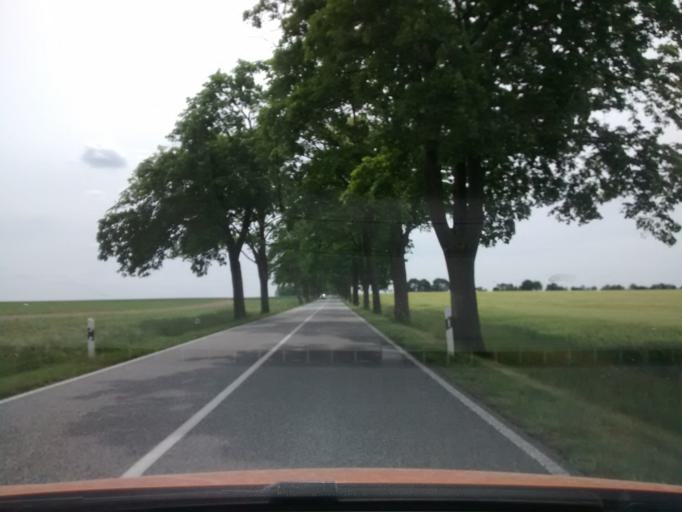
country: DE
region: Brandenburg
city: Juterbog
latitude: 51.9497
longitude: 13.1157
